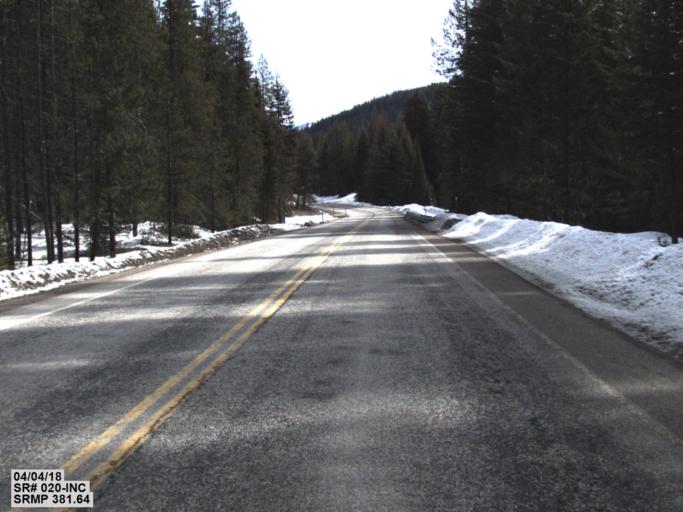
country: US
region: Washington
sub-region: Stevens County
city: Colville
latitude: 48.6403
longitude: -117.5239
